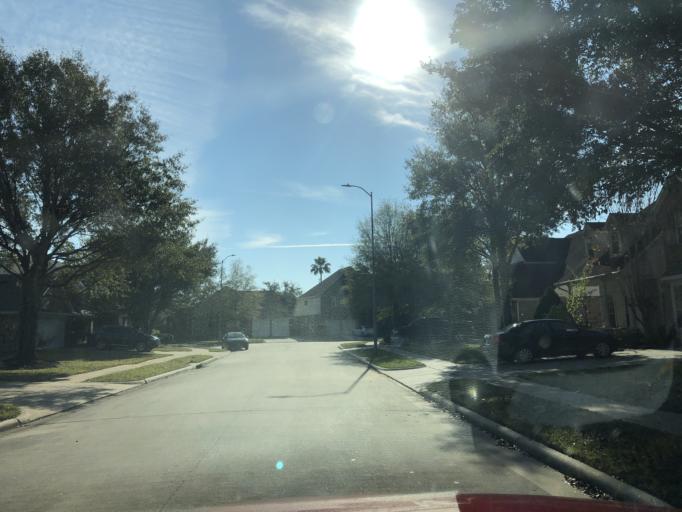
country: US
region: Texas
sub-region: Harris County
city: Tomball
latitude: 30.0325
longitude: -95.5613
